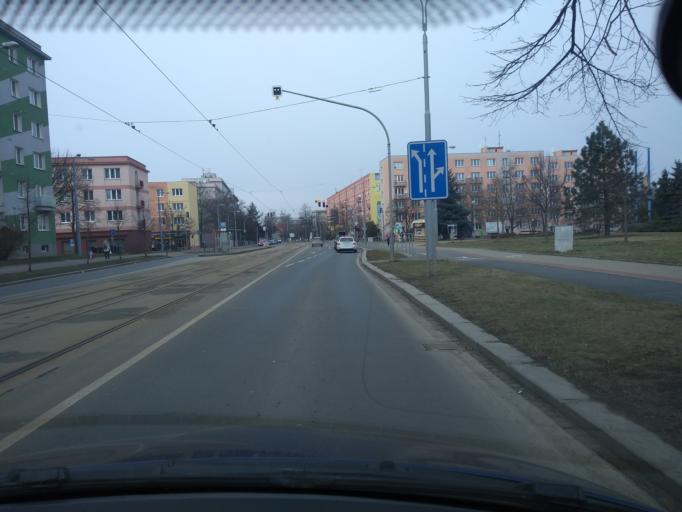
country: CZ
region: Plzensky
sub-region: Okres Plzen-Mesto
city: Pilsen
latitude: 49.7359
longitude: 13.3972
